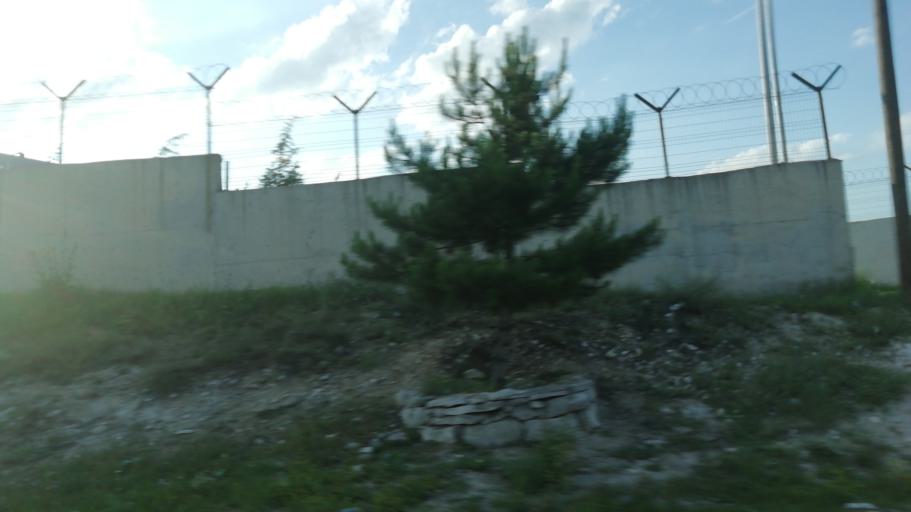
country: TR
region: Karabuk
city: Karabuk
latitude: 41.1342
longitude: 32.6324
